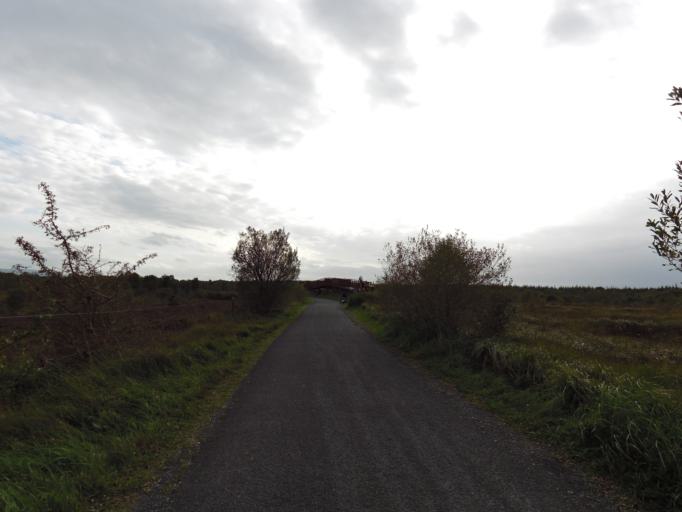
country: IE
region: Leinster
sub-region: Uibh Fhaili
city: Ferbane
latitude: 53.2210
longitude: -7.7323
